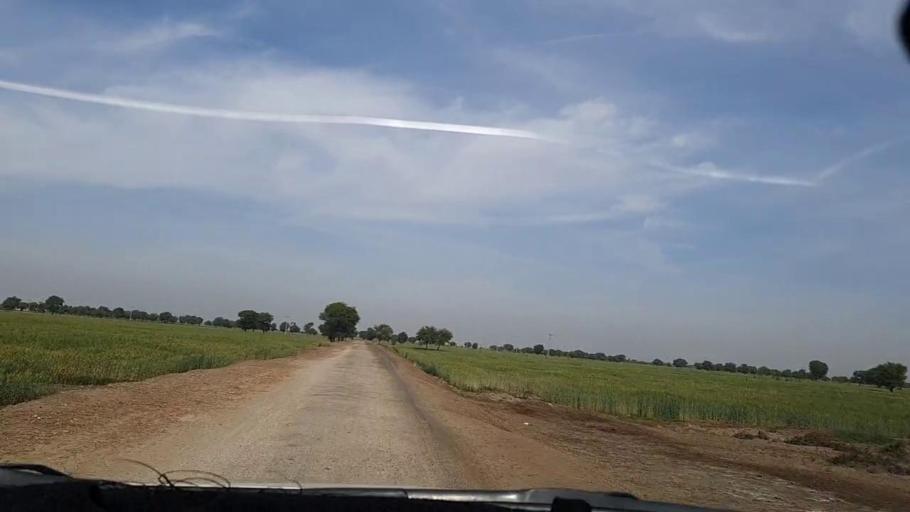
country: PK
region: Sindh
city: Dhoro Naro
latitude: 25.4465
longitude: 69.4972
